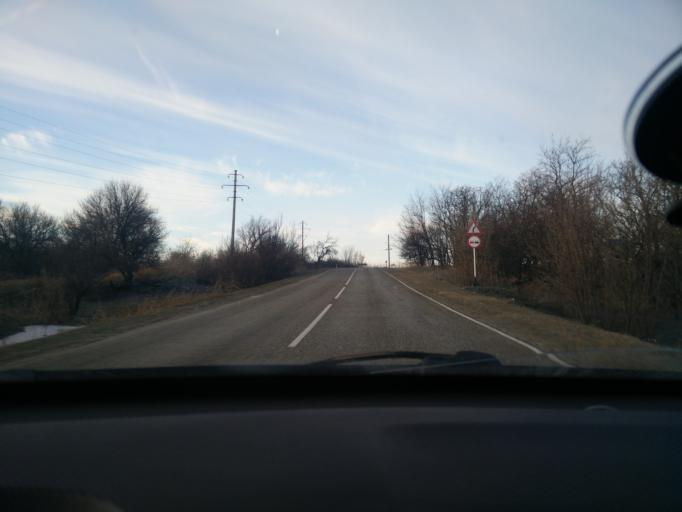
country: RU
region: Stavropol'skiy
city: Balakhonovskoye
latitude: 44.9805
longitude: 41.6925
